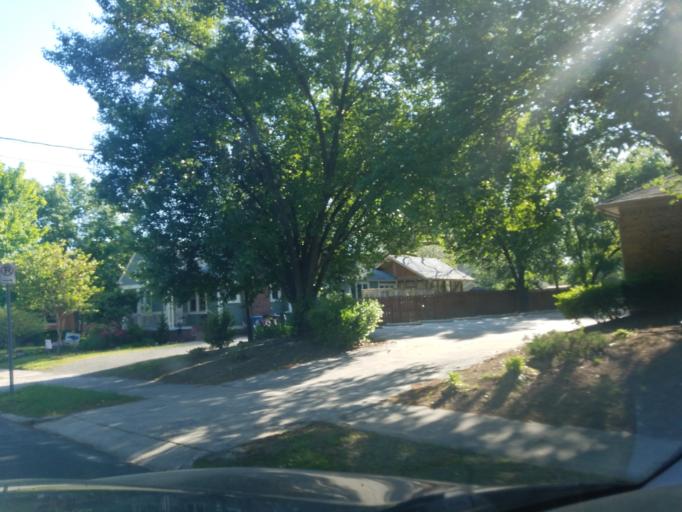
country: US
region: North Carolina
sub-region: Durham County
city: Durham
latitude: 36.0151
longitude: -78.9193
